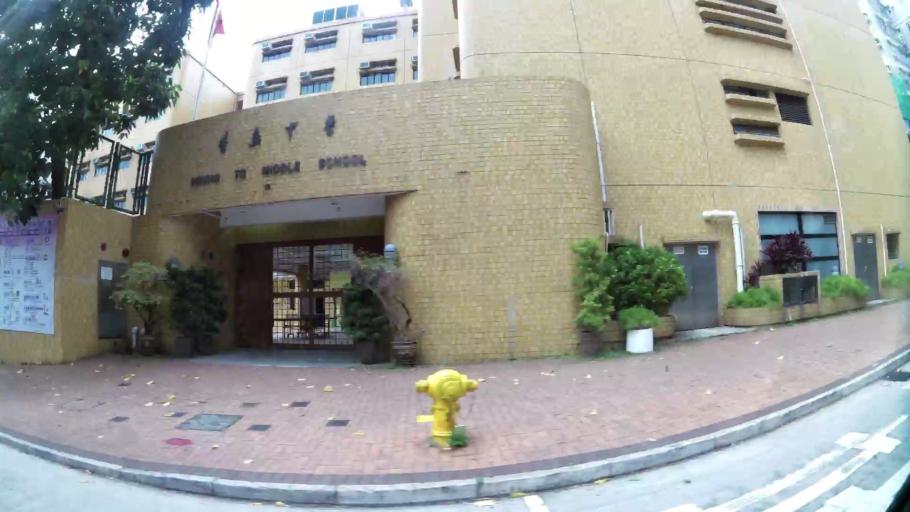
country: HK
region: Sham Shui Po
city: Sham Shui Po
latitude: 22.3352
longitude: 114.1743
